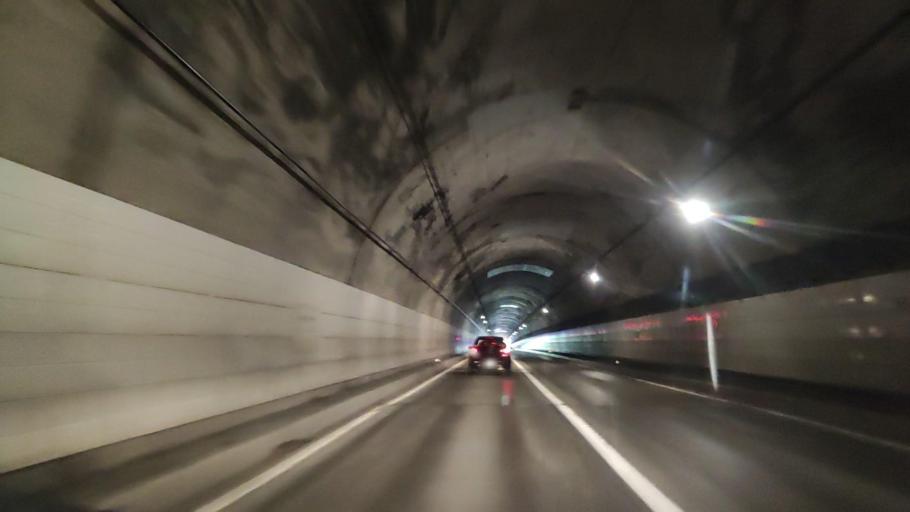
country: JP
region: Akita
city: Takanosu
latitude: 40.2129
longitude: 140.2183
